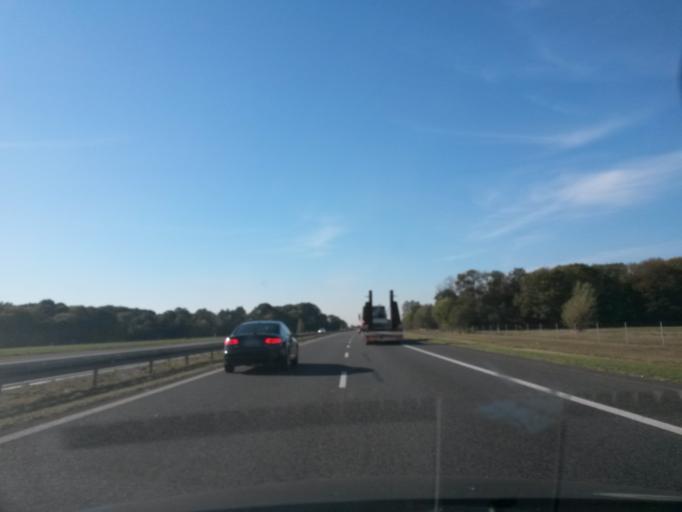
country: PL
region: Opole Voivodeship
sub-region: Powiat brzeski
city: Grodkow
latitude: 50.7729
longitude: 17.3709
